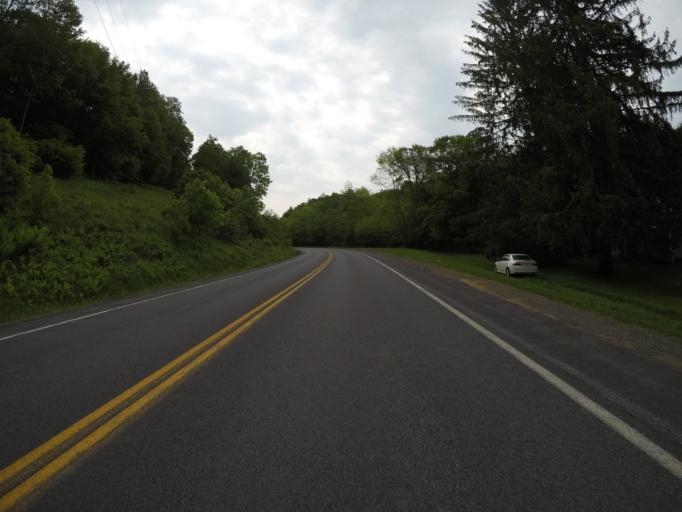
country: US
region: New York
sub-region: Sullivan County
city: Livingston Manor
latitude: 42.0661
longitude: -74.9428
